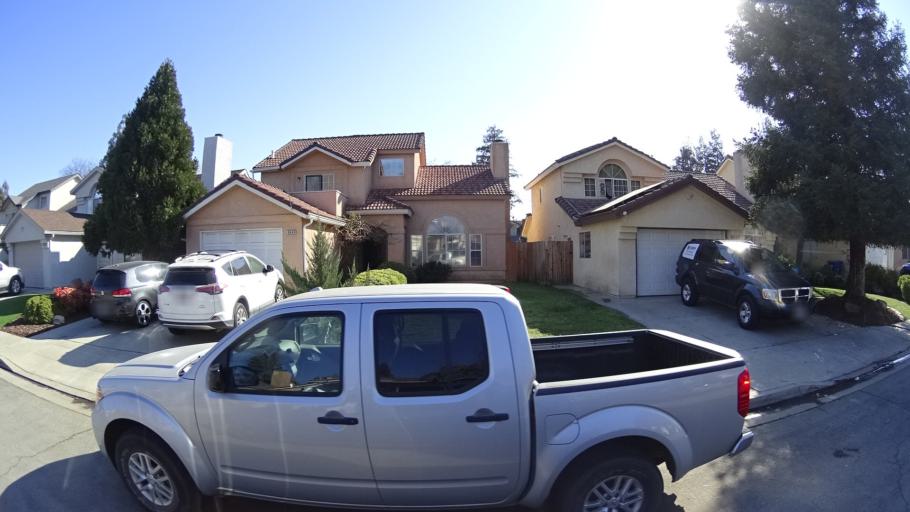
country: US
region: California
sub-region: Fresno County
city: Clovis
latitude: 36.8763
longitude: -119.7582
